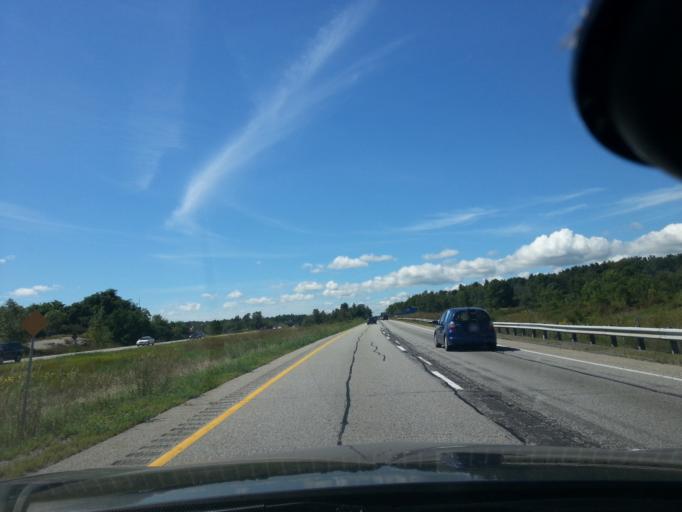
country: CA
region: Ontario
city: Gananoque
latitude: 44.3433
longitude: -76.1373
